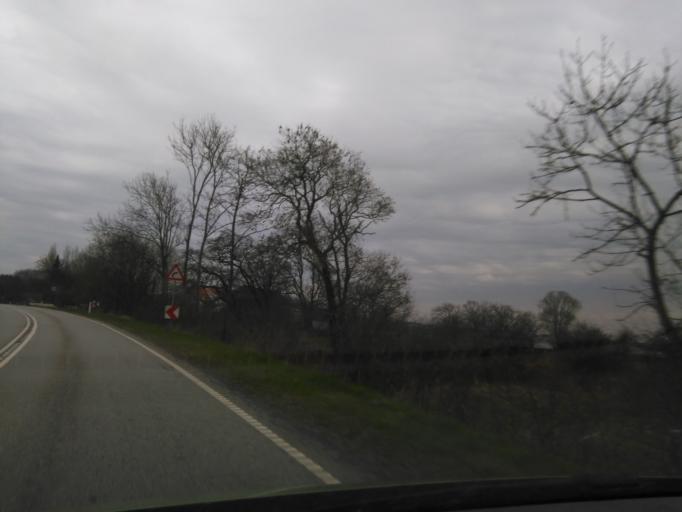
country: DK
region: North Denmark
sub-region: Mariagerfjord Kommune
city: Hadsund
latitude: 56.6908
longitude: 10.1040
